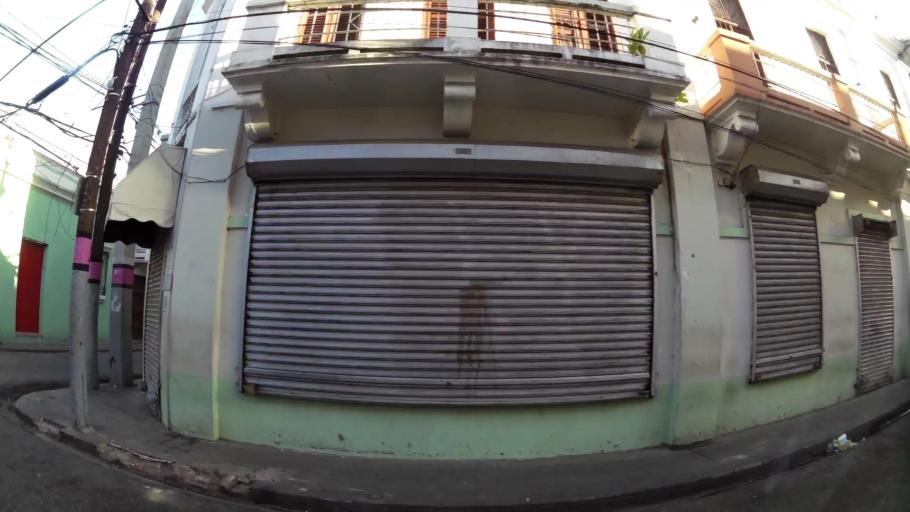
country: DO
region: Nacional
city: Ciudad Nueva
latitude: 18.4714
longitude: -69.8900
